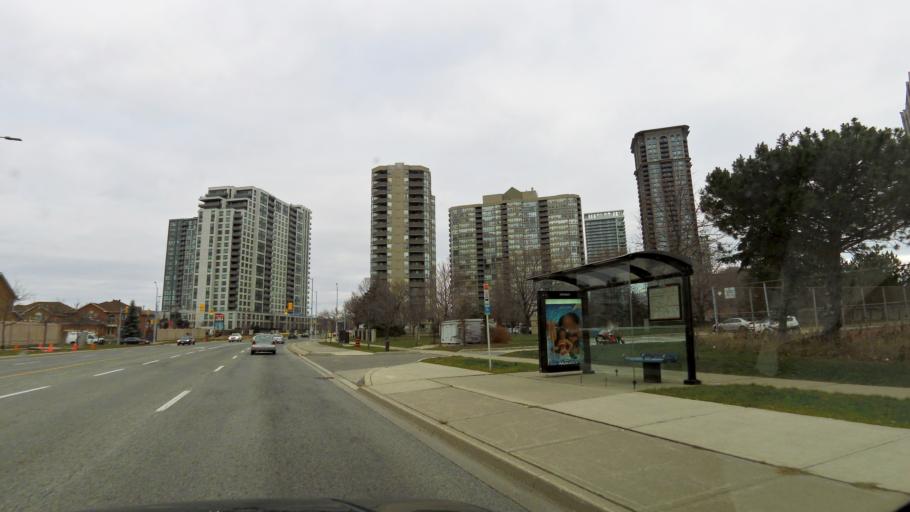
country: CA
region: Ontario
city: Mississauga
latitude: 43.5874
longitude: -79.6526
